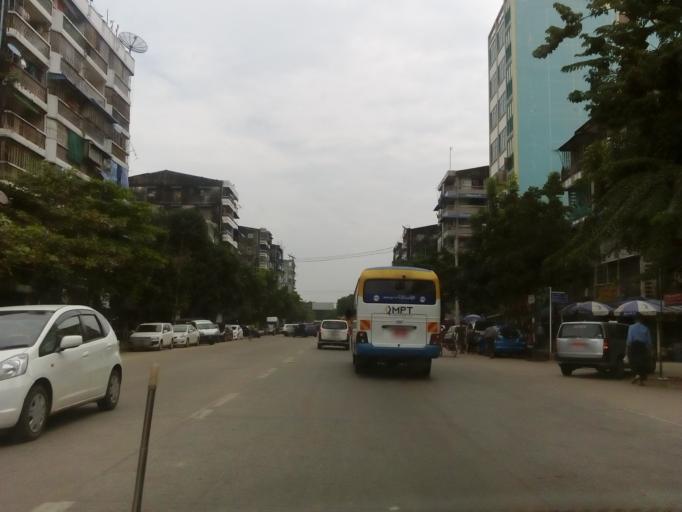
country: MM
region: Yangon
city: Yangon
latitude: 16.8086
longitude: 96.1782
